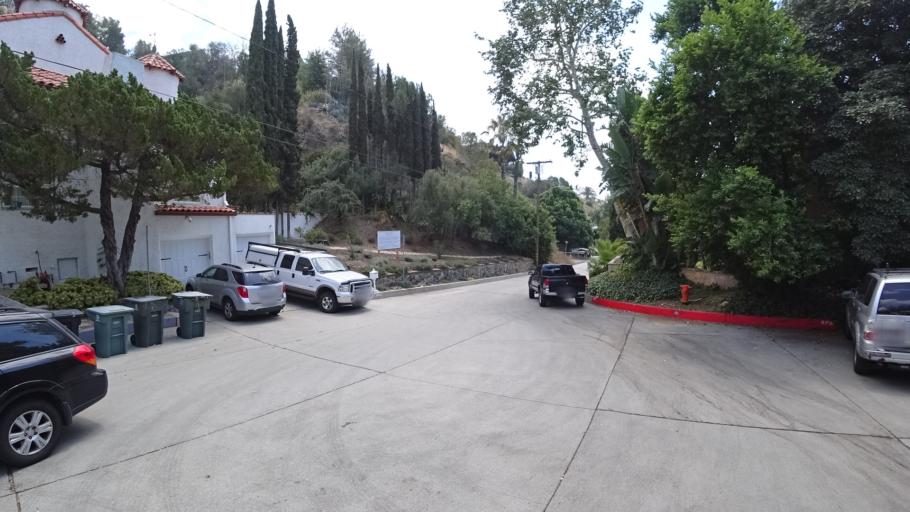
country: US
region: California
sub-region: Los Angeles County
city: Burbank
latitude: 34.1902
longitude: -118.2860
